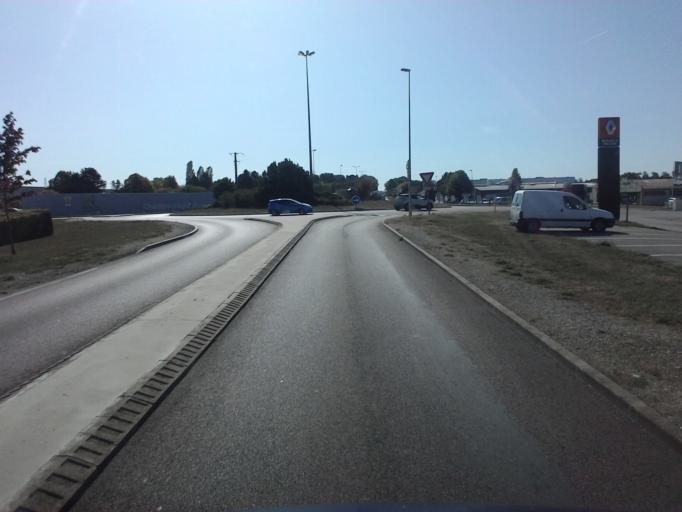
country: FR
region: Bourgogne
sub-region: Departement de la Cote-d'Or
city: Chatillon-sur-Seine
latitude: 47.8791
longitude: 4.5664
